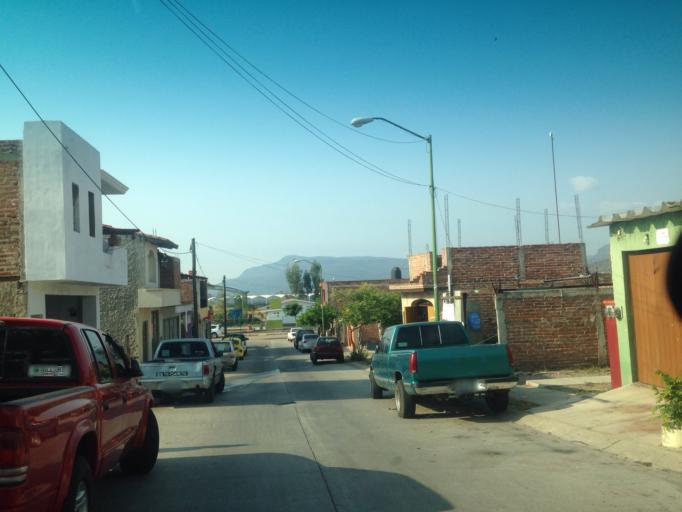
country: MX
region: Jalisco
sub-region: Atotonilco el Alto
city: Vistas del Maguey [Fraccionamiento]
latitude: 20.5282
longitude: -102.5284
